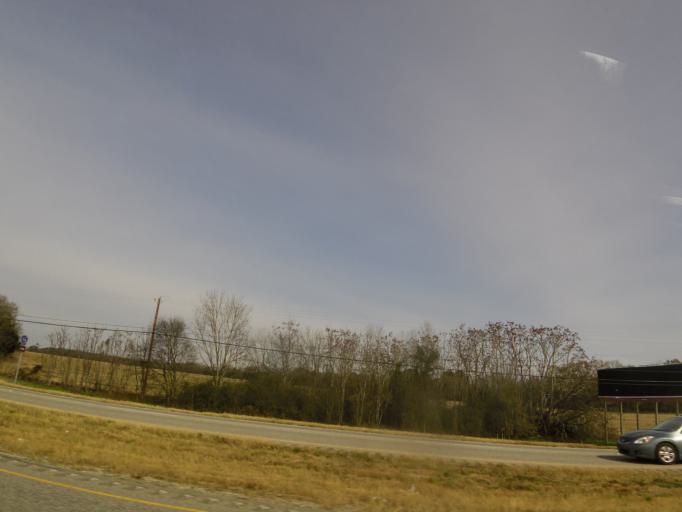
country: US
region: Alabama
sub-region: Dale County
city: Midland City
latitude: 31.2934
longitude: -85.4765
